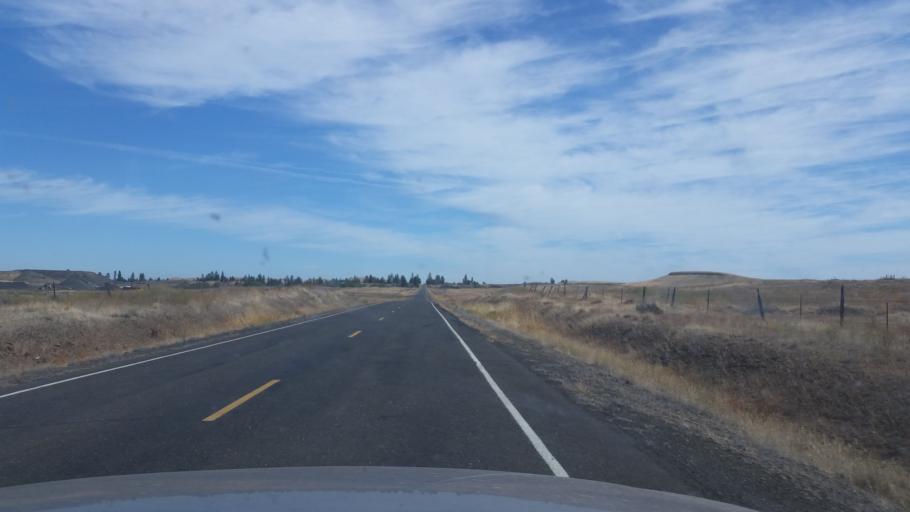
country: US
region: Washington
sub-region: Spokane County
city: Medical Lake
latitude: 47.3295
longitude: -117.8892
